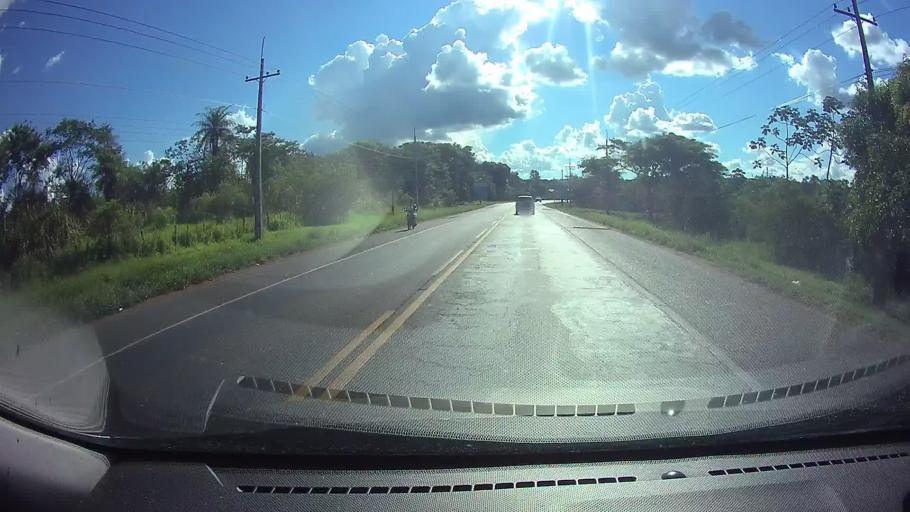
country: PY
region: Cordillera
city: Eusebio Ayala
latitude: -25.3822
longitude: -57.0060
